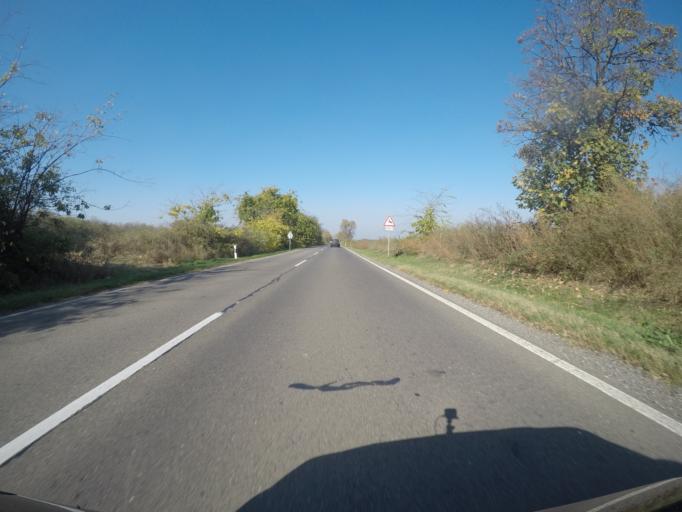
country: HU
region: Tolna
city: Tengelic
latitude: 46.5250
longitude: 18.6593
